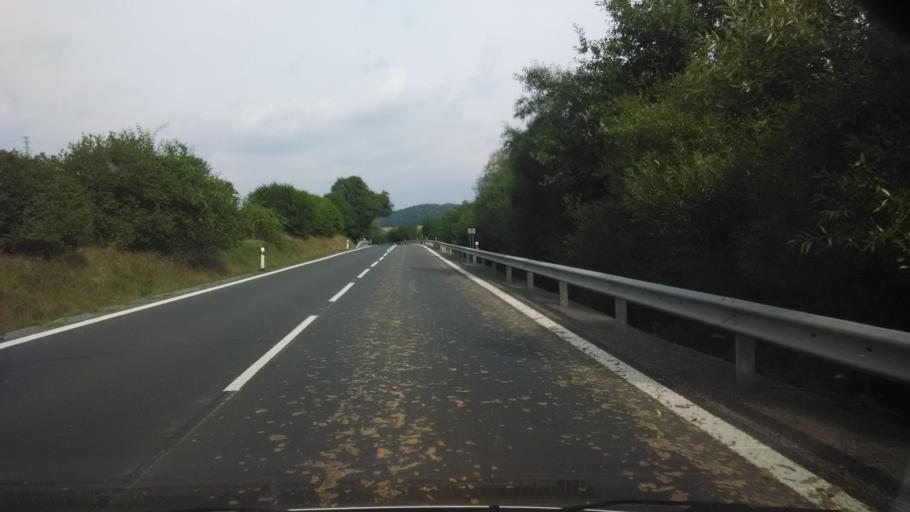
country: SK
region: Banskobystricky
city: Krupina
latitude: 48.3202
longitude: 19.0545
